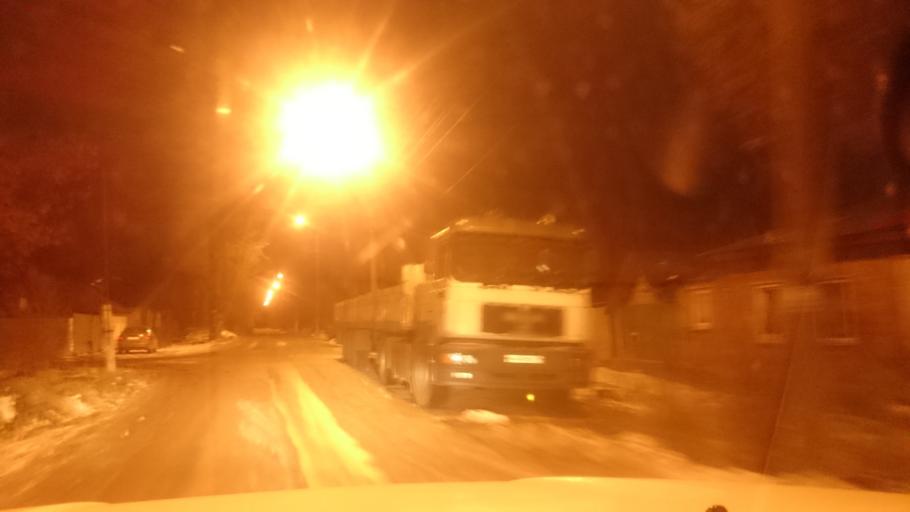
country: RU
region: Tula
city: Tula
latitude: 54.1865
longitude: 37.6319
